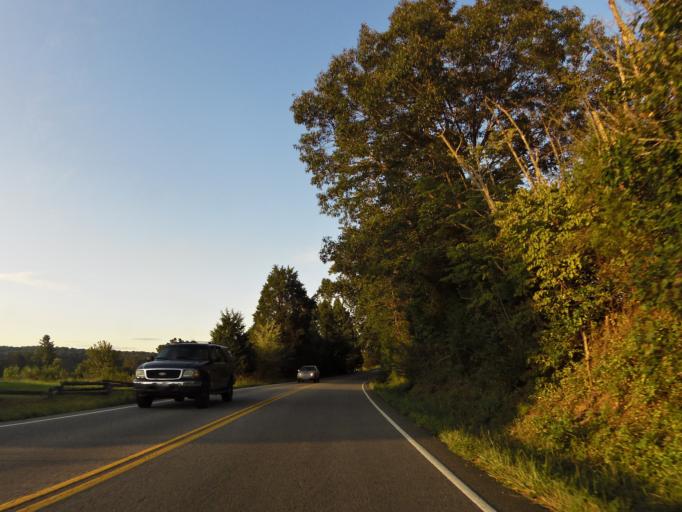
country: US
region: Tennessee
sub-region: Roane County
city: Midtown
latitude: 35.8545
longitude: -84.5401
